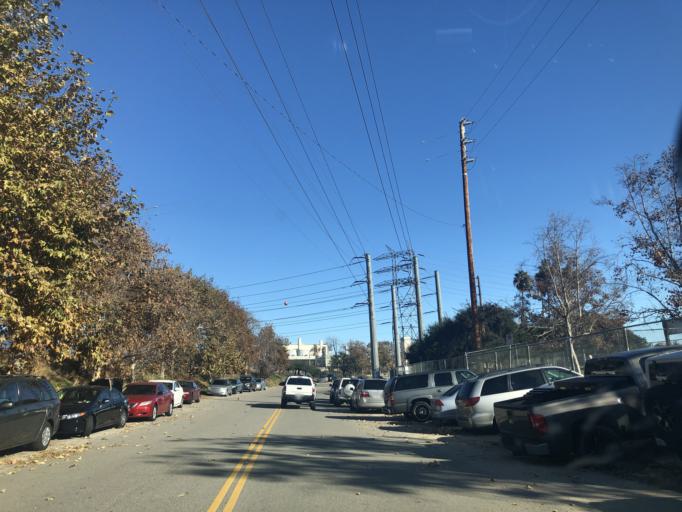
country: US
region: California
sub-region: Los Angeles County
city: North Glendale
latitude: 34.1556
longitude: -118.2833
